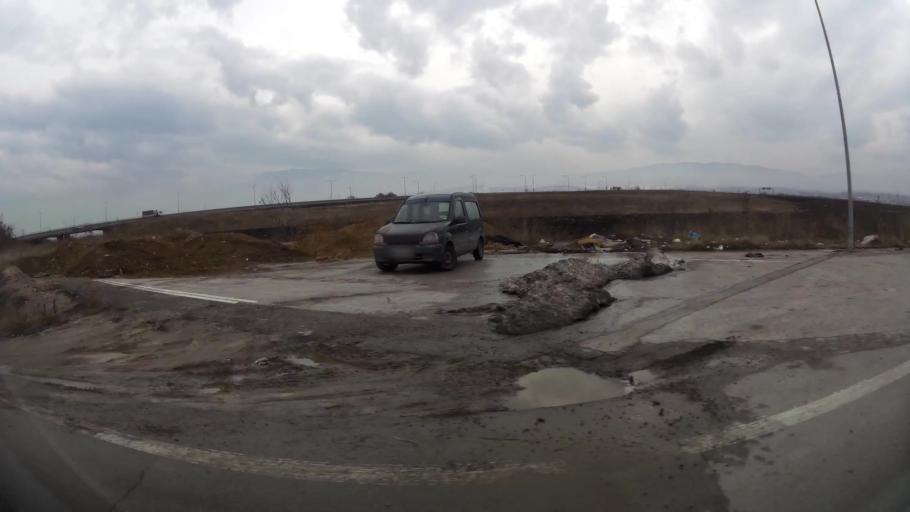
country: BG
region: Sofiya
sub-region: Obshtina Bozhurishte
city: Bozhurishte
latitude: 42.7135
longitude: 23.2276
